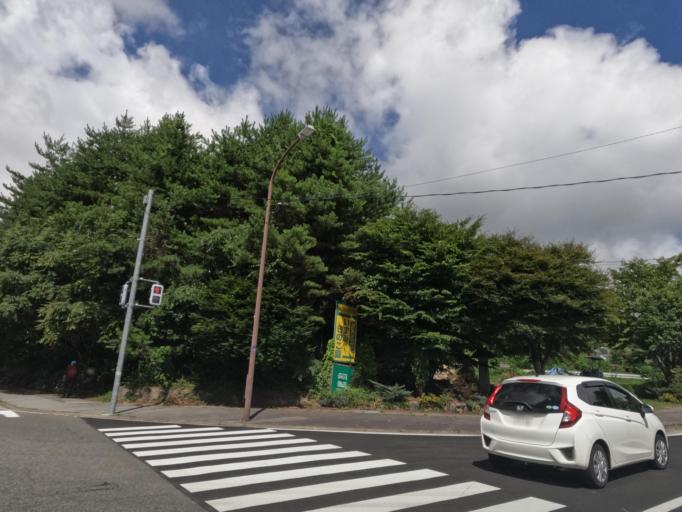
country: JP
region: Yamanashi
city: Nirasaki
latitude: 35.8866
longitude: 138.4116
